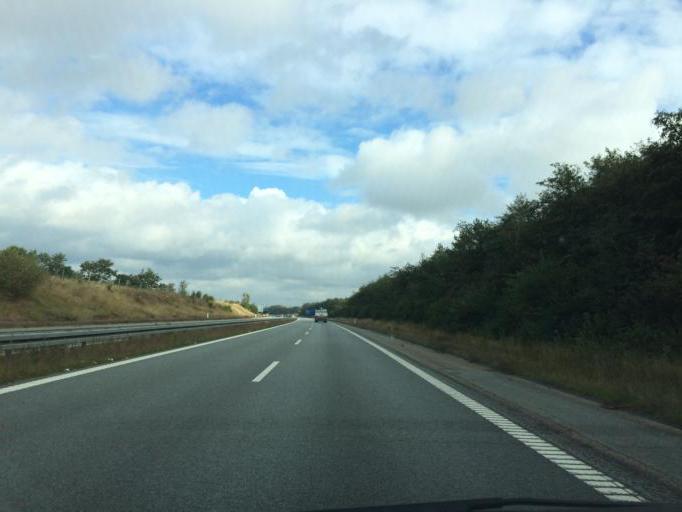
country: DK
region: North Denmark
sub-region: Bronderslev Kommune
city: Hjallerup
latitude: 57.1617
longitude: 10.1815
